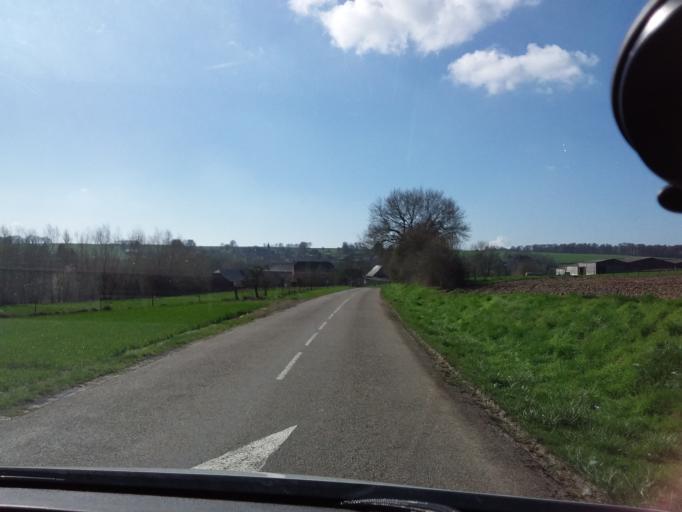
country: FR
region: Picardie
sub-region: Departement de l'Aisne
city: Montcornet
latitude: 49.7874
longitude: 4.0056
